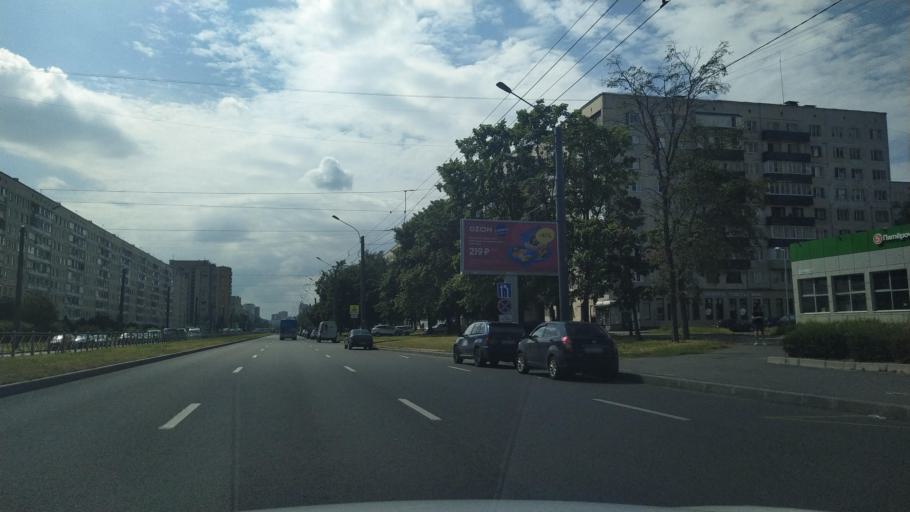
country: RU
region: Leningrad
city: Parnas
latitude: 60.0526
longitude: 30.3570
